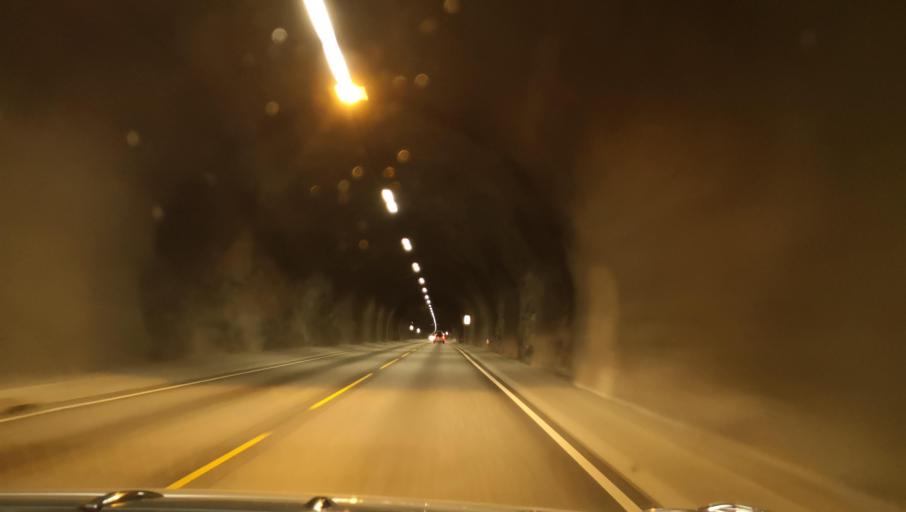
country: NO
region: Hordaland
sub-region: Granvin
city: Granvin
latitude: 60.5837
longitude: 6.6184
